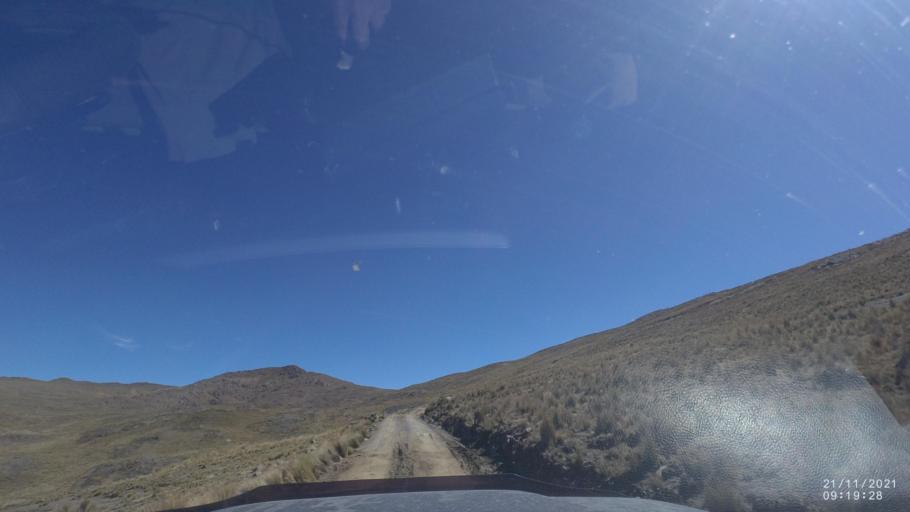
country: BO
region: Cochabamba
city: Cochabamba
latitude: -17.1144
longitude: -66.2531
